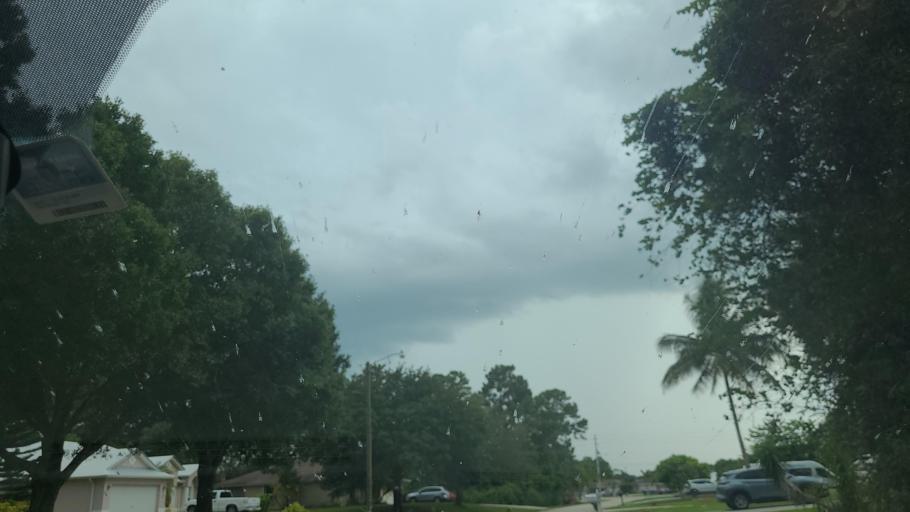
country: US
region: Florida
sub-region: Saint Lucie County
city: Port Saint Lucie
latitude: 27.2489
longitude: -80.4025
